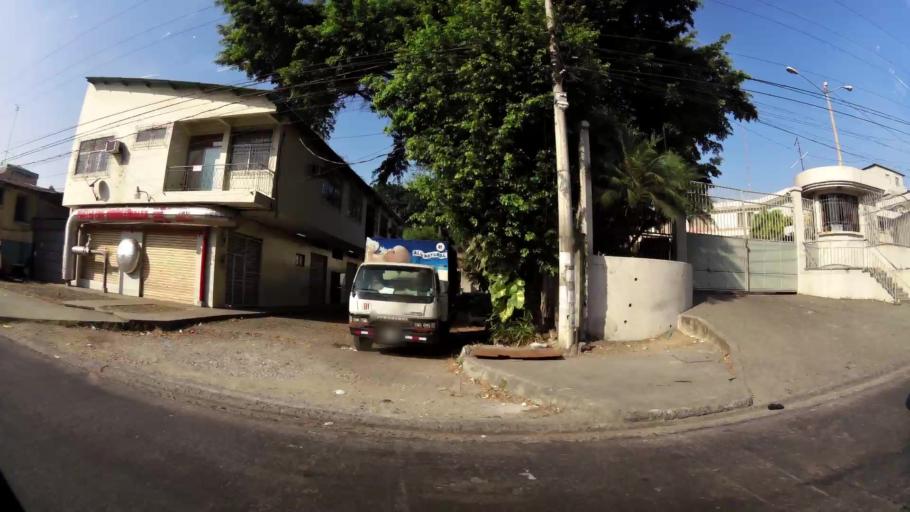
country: EC
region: Guayas
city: Guayaquil
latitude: -2.1472
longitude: -79.9332
